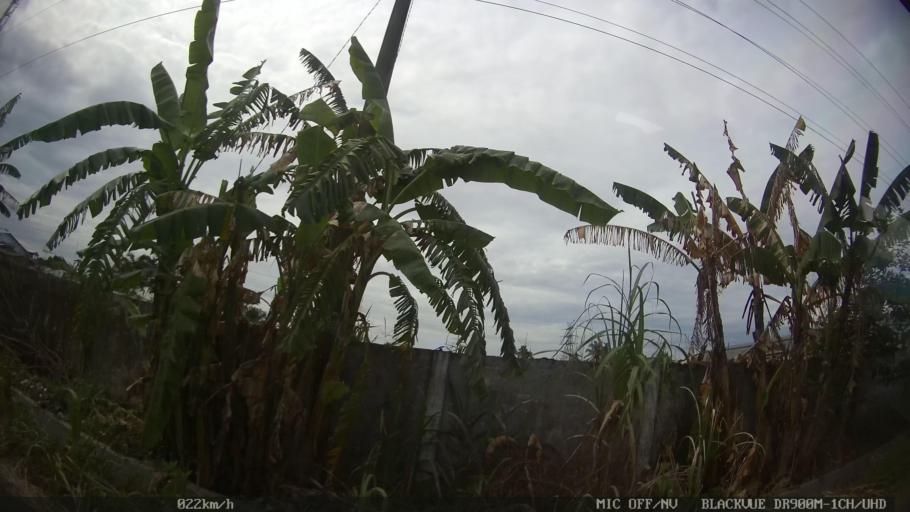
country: ID
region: North Sumatra
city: Sunggal
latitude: 3.5894
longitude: 98.5785
